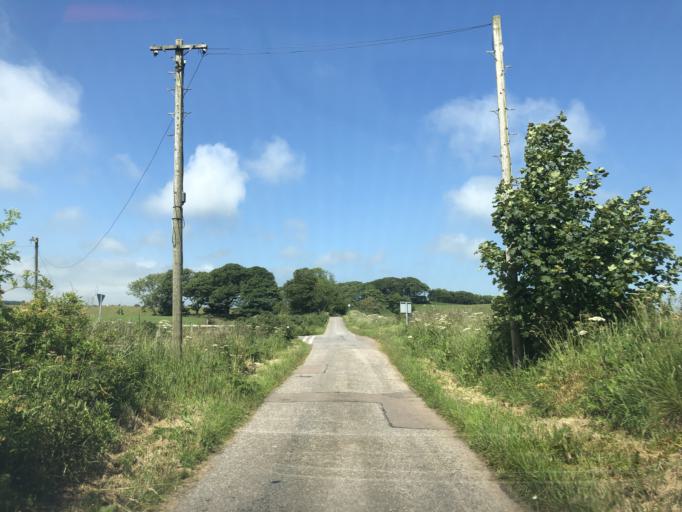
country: GB
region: Scotland
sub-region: Aberdeenshire
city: Stonehaven
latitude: 56.9157
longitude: -2.2043
